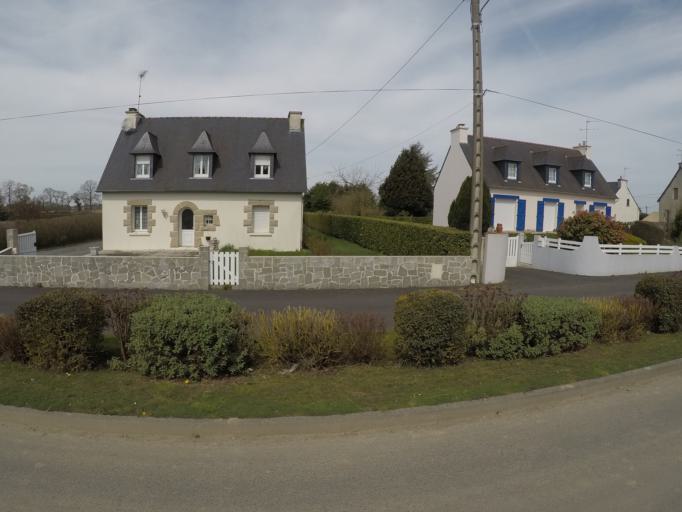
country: FR
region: Brittany
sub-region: Departement des Cotes-d'Armor
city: Plelo
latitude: 48.5478
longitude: -2.9613
